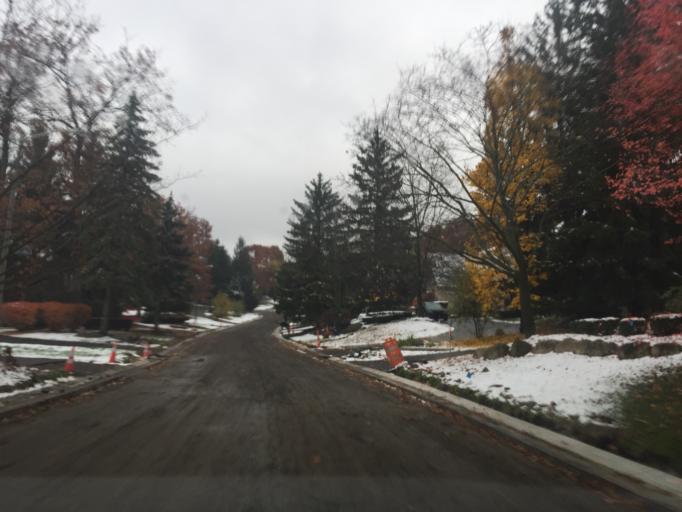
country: US
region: Michigan
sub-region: Oakland County
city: Bloomfield Hills
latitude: 42.5986
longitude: -83.2762
